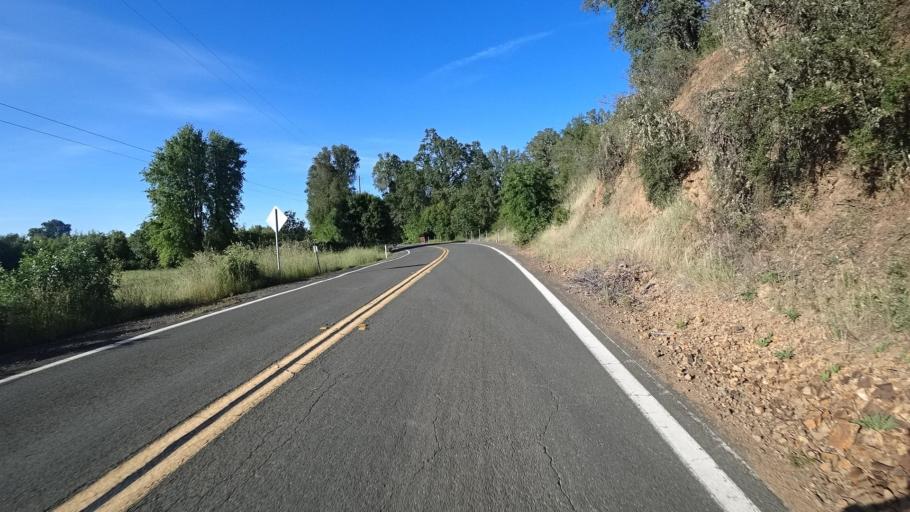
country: US
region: California
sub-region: Lake County
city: North Lakeport
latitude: 39.0893
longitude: -122.9496
